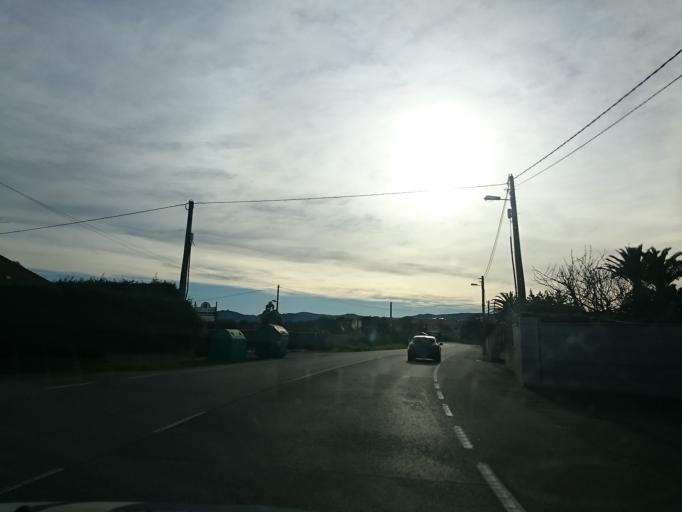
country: ES
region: Asturias
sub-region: Province of Asturias
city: Arriba
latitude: 43.5212
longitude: -5.5910
